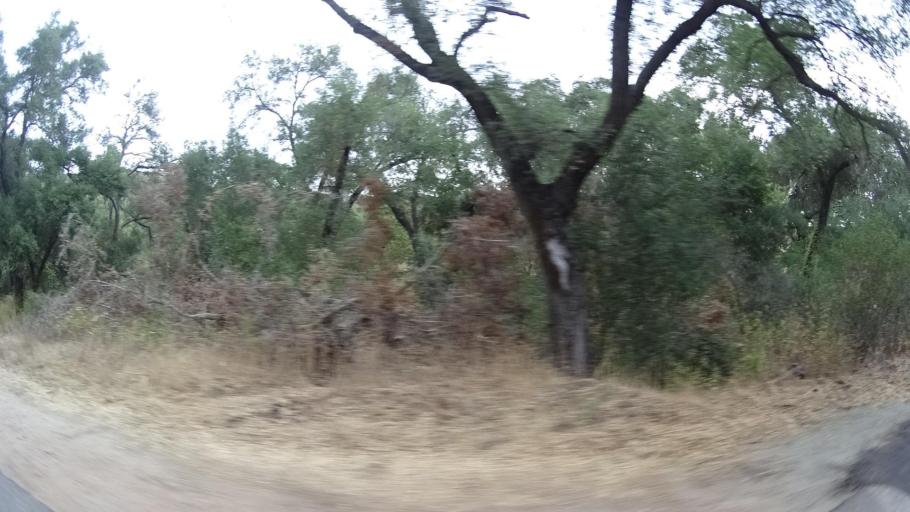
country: US
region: California
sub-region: San Diego County
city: Ramona
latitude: 32.9867
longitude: -116.9258
